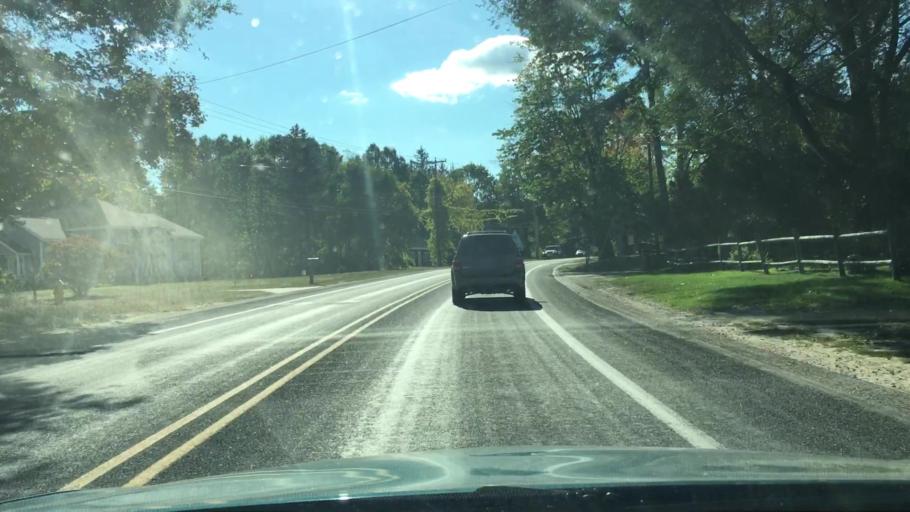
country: US
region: Michigan
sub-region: Muskegon County
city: Muskegon Heights
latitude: 43.1954
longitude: -86.1838
